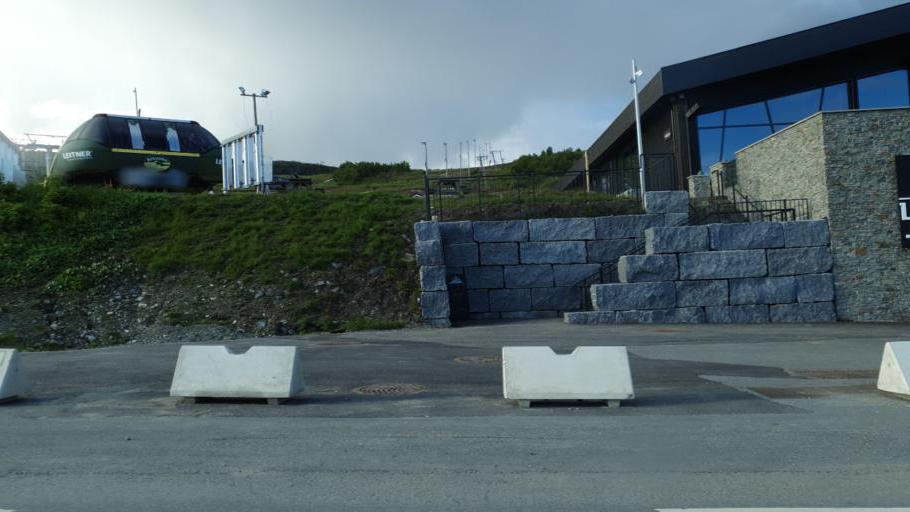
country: NO
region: Oppland
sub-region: Vestre Slidre
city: Slidre
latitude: 61.2491
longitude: 8.9047
